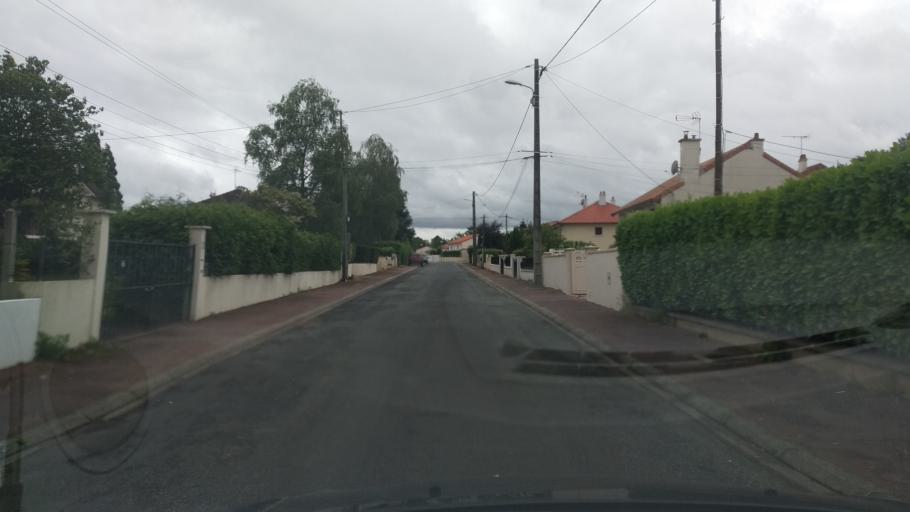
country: FR
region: Poitou-Charentes
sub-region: Departement de la Vienne
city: Vouneuil-sous-Biard
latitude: 46.6026
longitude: 0.2774
